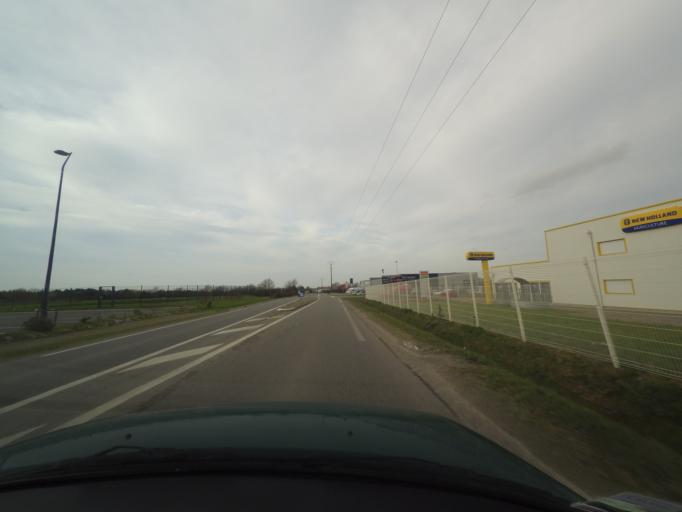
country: FR
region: Pays de la Loire
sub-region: Departement de la Loire-Atlantique
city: Saint-Pere-en-Retz
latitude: 47.1961
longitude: -2.0297
